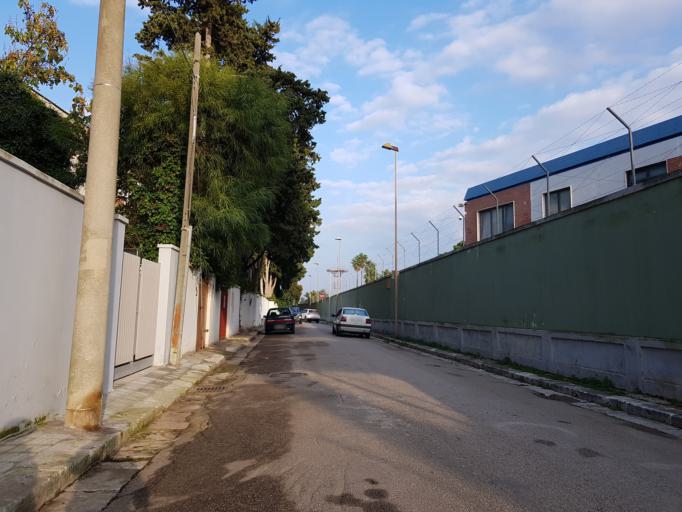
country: IT
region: Apulia
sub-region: Provincia di Brindisi
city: Materdomini
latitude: 40.6484
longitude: 17.9478
